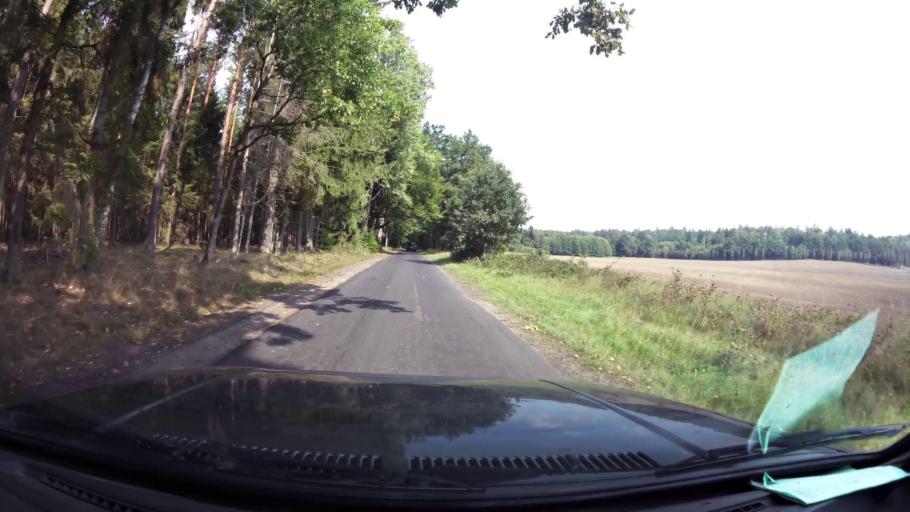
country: PL
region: West Pomeranian Voivodeship
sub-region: Powiat koszalinski
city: Bobolice
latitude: 54.0947
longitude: 16.4878
